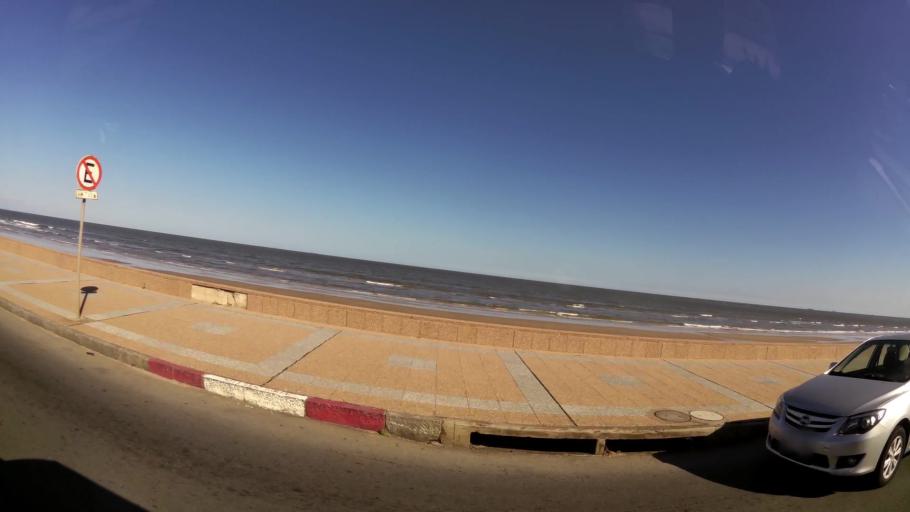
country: UY
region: Canelones
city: Barra de Carrasco
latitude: -34.8961
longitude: -56.0611
